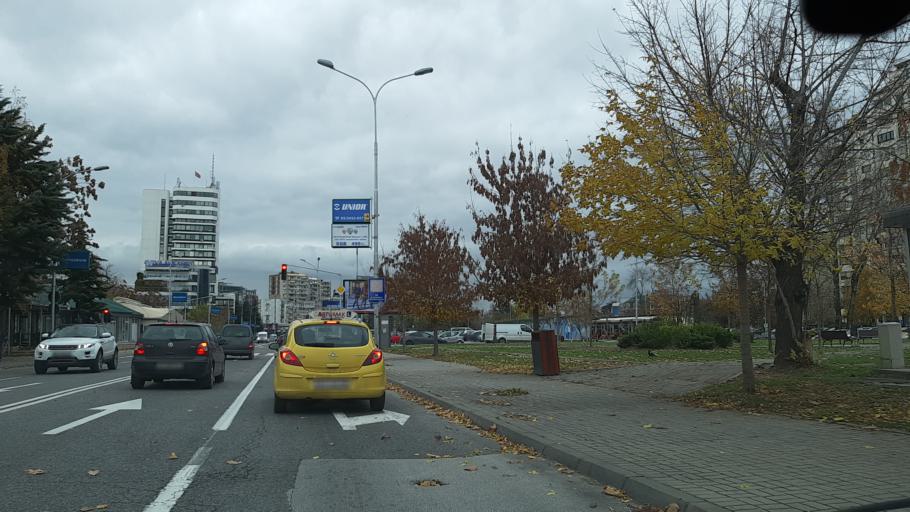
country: MK
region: Karpos
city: Skopje
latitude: 41.9940
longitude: 21.4206
